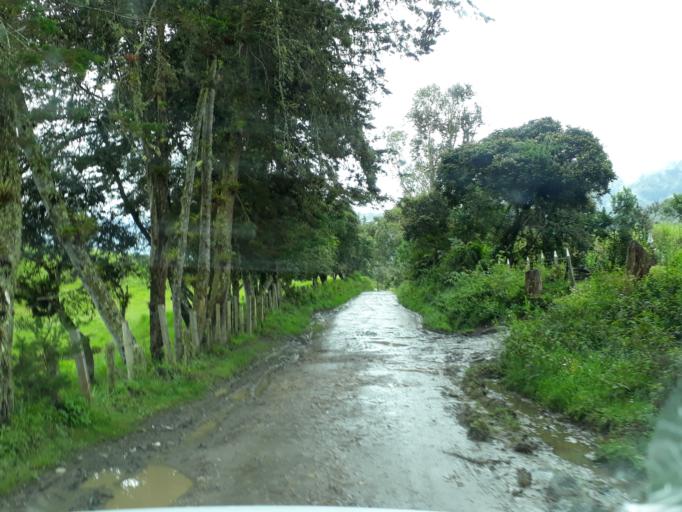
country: CO
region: Cundinamarca
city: Gacheta
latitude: 4.8586
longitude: -73.6387
